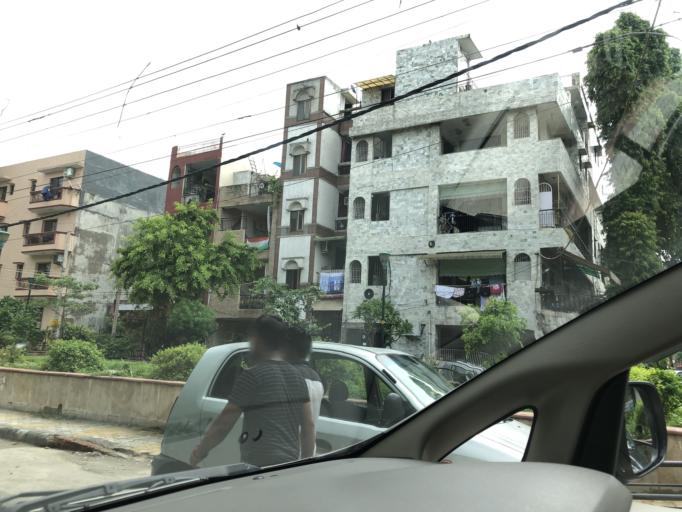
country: IN
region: NCT
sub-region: New Delhi
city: New Delhi
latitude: 28.5719
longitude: 77.2407
